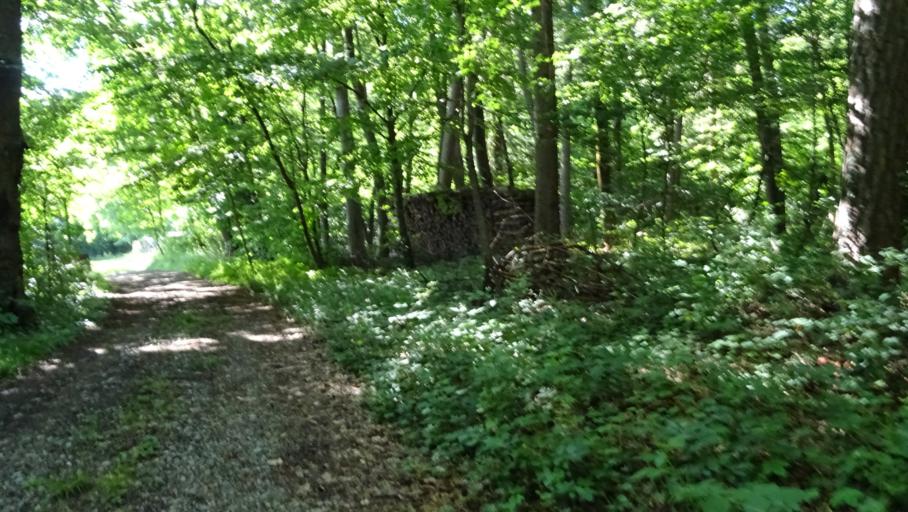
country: DE
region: Baden-Wuerttemberg
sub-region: Karlsruhe Region
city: Obrigheim
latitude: 49.3769
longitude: 9.1162
